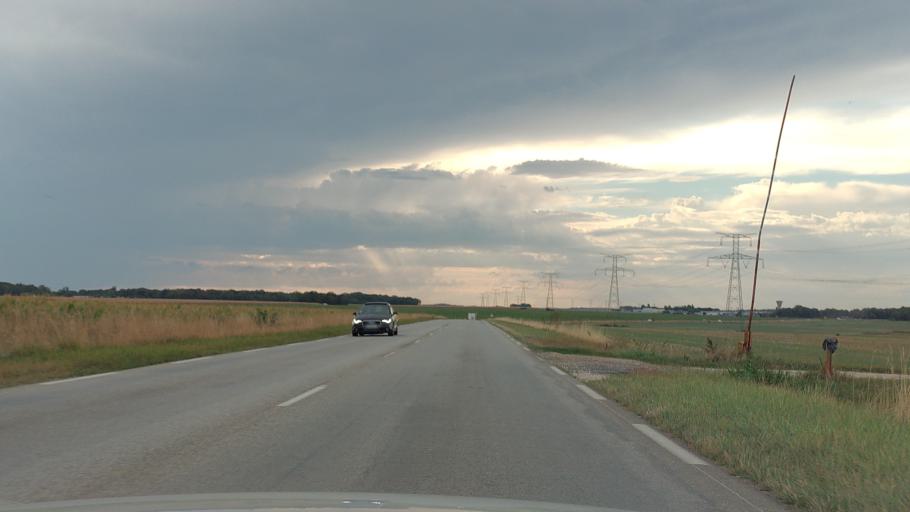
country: FR
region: Ile-de-France
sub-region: Departement de Seine-et-Marne
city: Guignes
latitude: 48.6218
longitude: 2.8383
